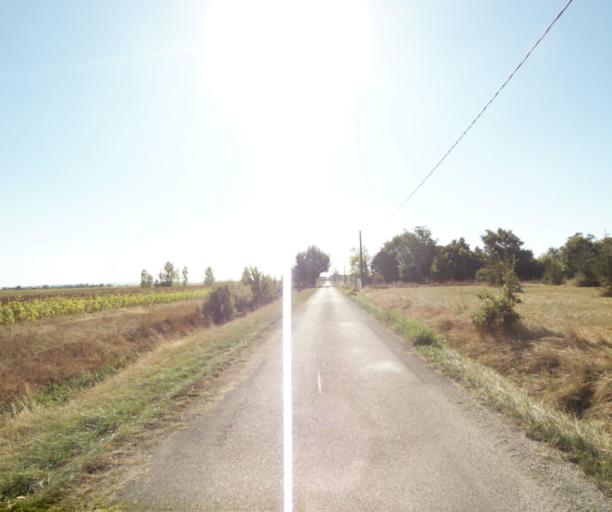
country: FR
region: Midi-Pyrenees
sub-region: Departement du Tarn-et-Garonne
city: Verdun-sur-Garonne
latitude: 43.8389
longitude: 1.2132
